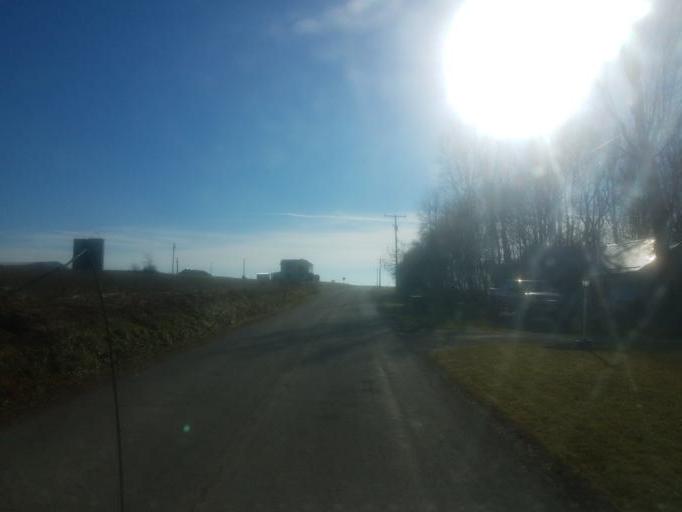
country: US
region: Ohio
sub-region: Richland County
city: Ontario
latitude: 40.7294
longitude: -82.6354
